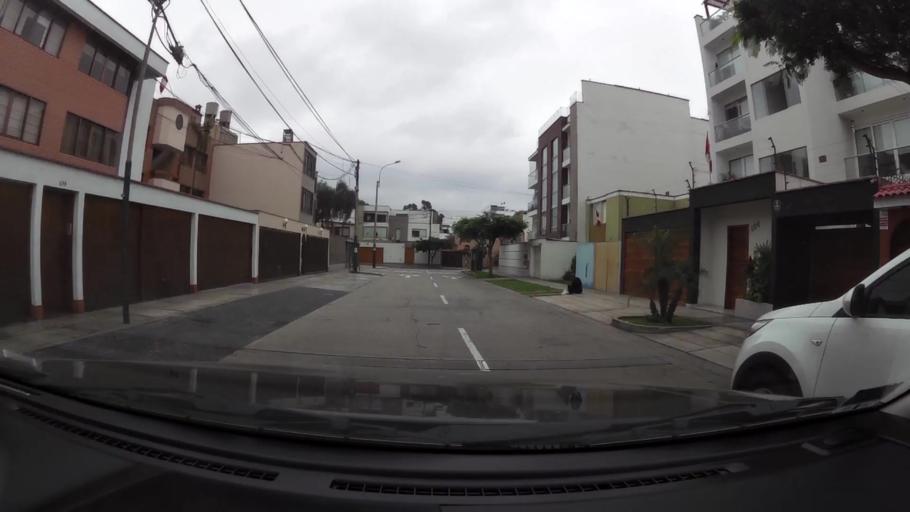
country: PE
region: Lima
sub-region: Lima
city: Surco
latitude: -12.1194
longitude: -76.9914
